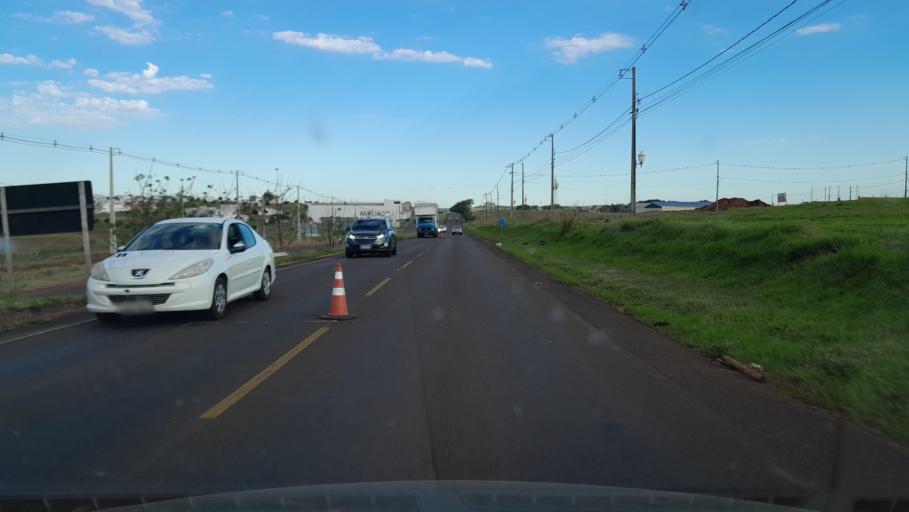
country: BR
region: Parana
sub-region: Umuarama
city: Umuarama
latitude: -23.7559
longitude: -53.2719
